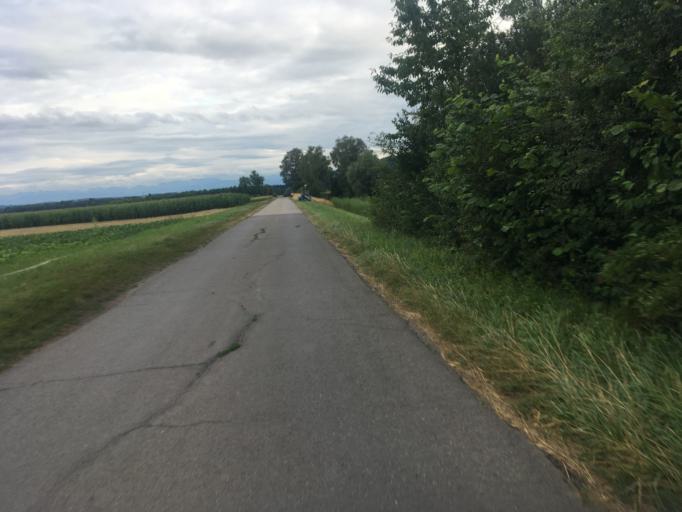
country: CH
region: Bern
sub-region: Seeland District
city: Ins
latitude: 46.9920
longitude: 7.1031
